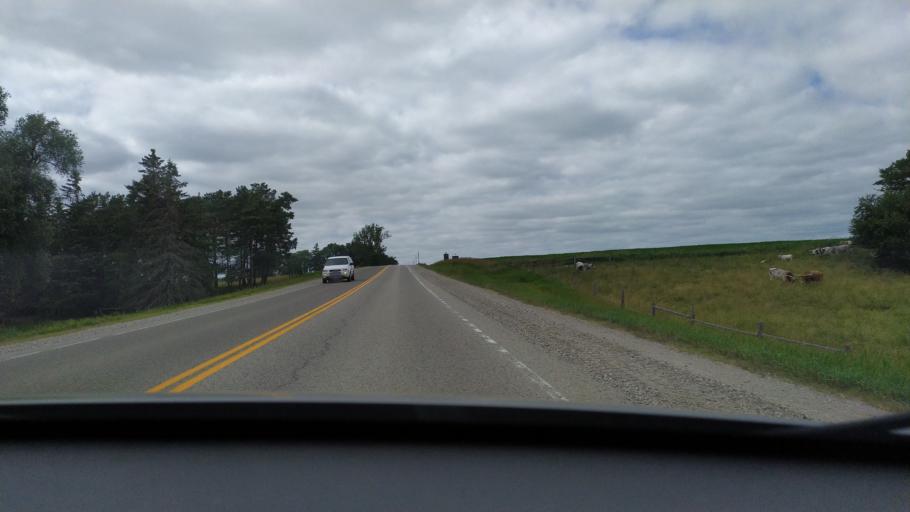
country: CA
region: Ontario
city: Stratford
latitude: 43.3267
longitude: -80.9576
